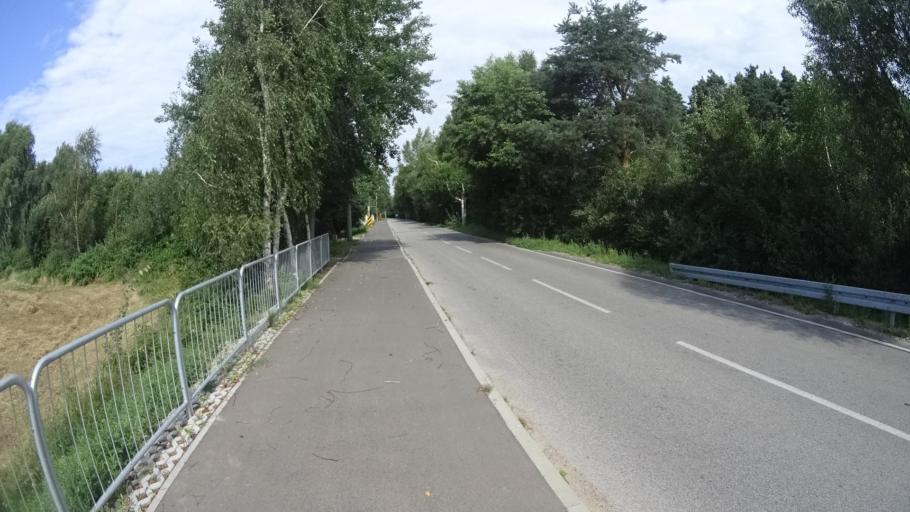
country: PL
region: Masovian Voivodeship
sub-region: Powiat piaseczynski
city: Tarczyn
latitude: 52.0162
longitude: 20.7955
